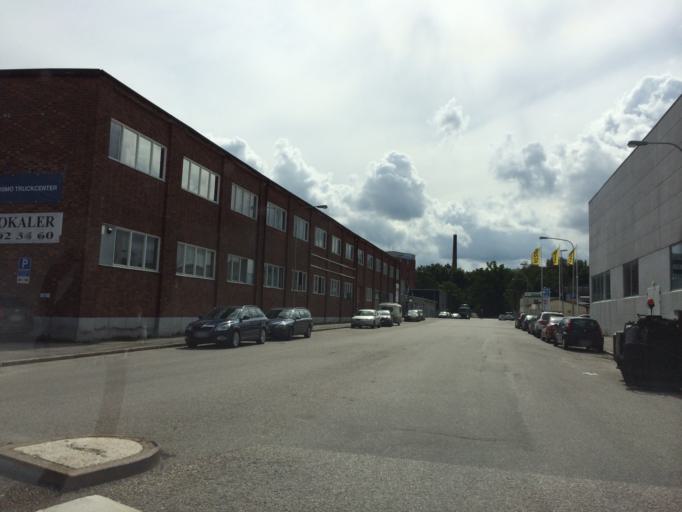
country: SE
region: Stockholm
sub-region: Stockholms Kommun
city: Arsta
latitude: 59.2935
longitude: 18.0059
